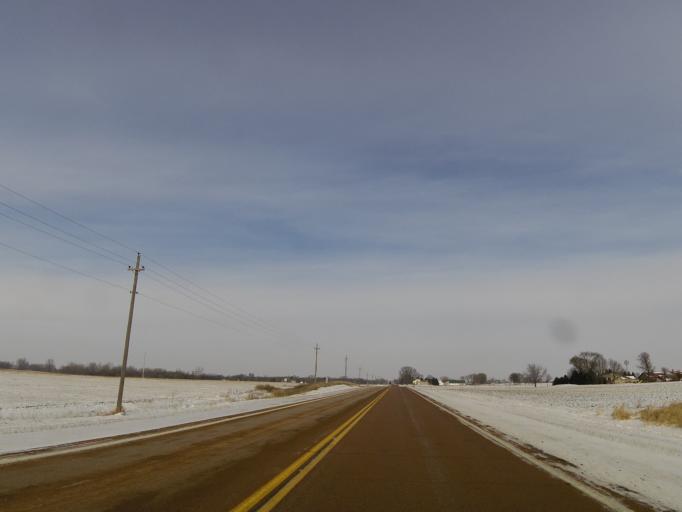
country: US
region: Minnesota
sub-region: McLeod County
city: Lester Prairie
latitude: 44.8946
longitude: -93.9713
